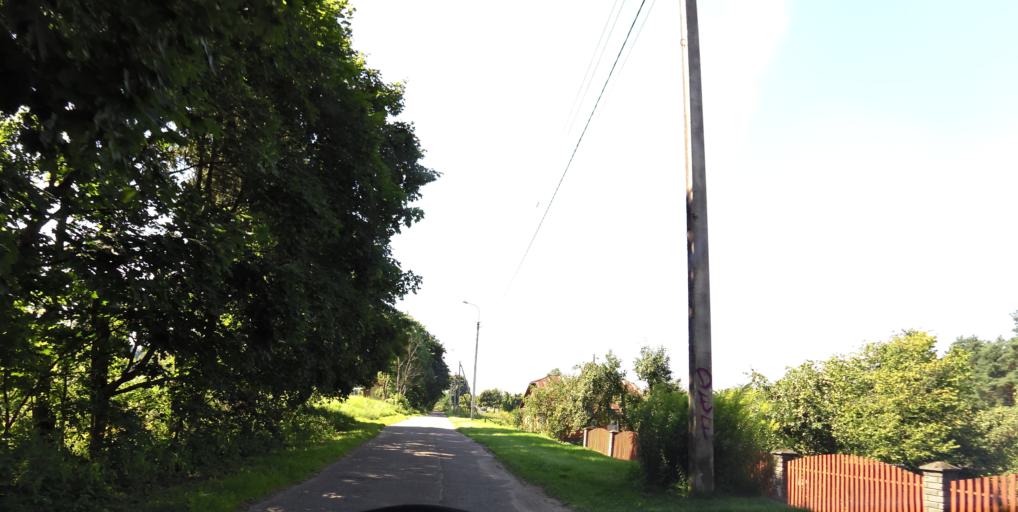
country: LT
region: Vilnius County
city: Rasos
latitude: 54.6793
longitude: 25.3556
